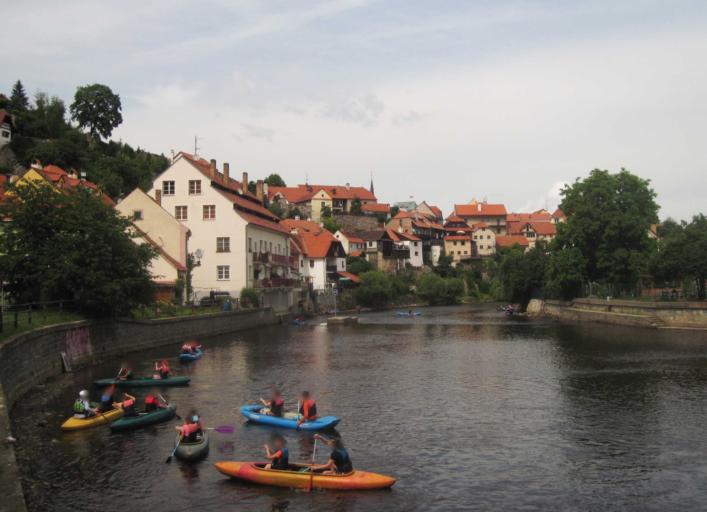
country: CZ
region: Jihocesky
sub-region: Okres Cesky Krumlov
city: Cesky Krumlov
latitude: 48.8054
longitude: 14.3125
